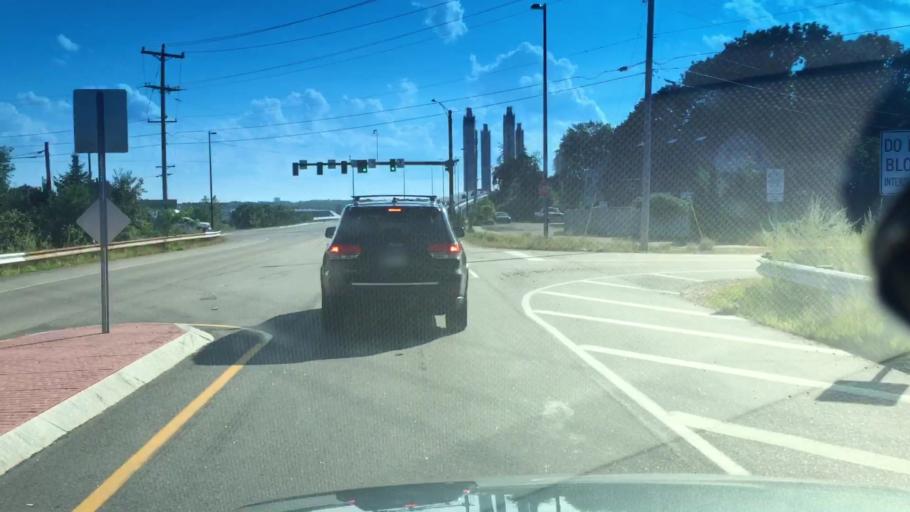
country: US
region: New Hampshire
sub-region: Rockingham County
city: Portsmouth
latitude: 43.0902
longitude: -70.7569
